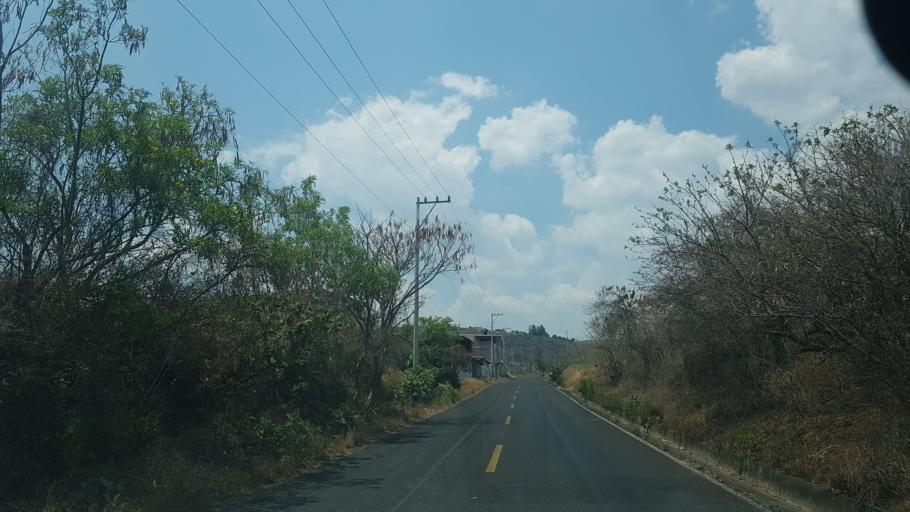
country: MX
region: Puebla
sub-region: Atzitzihuacan
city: Santiago Atzitzihuacan
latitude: 18.8332
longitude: -98.5917
